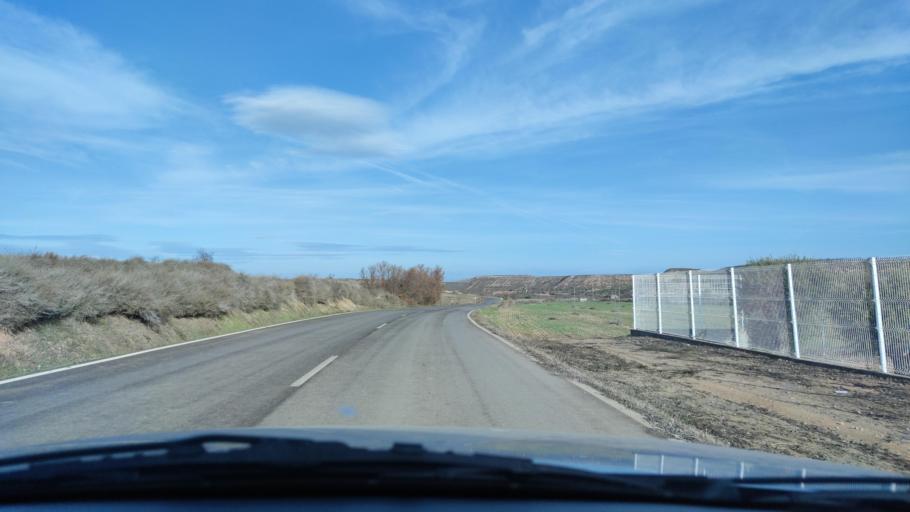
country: ES
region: Catalonia
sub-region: Provincia de Lleida
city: Alcano
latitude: 41.4848
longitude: 0.6161
